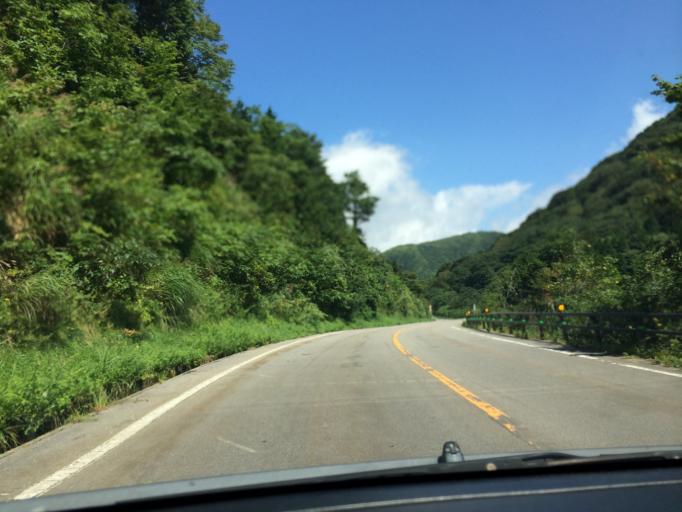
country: JP
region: Tottori
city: Kurayoshi
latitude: 35.3369
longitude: 133.5894
